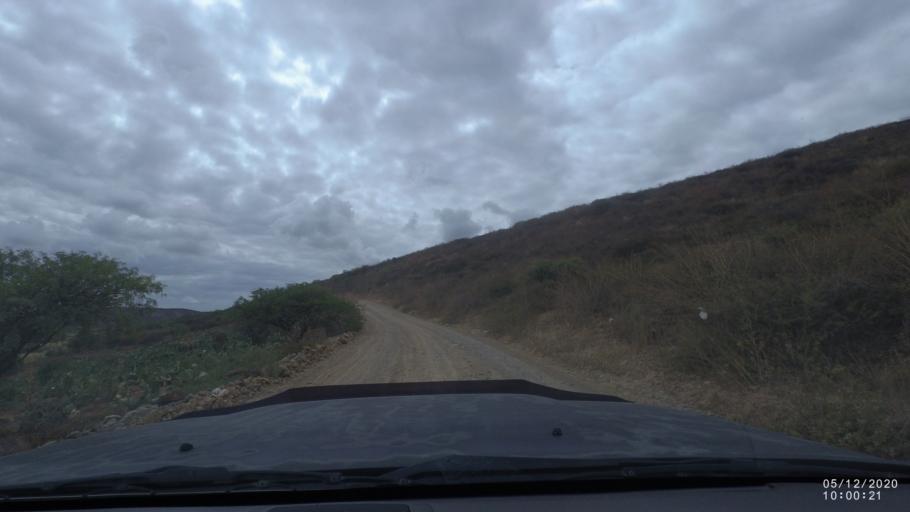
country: BO
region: Cochabamba
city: Sipe Sipe
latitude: -17.4370
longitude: -66.2890
